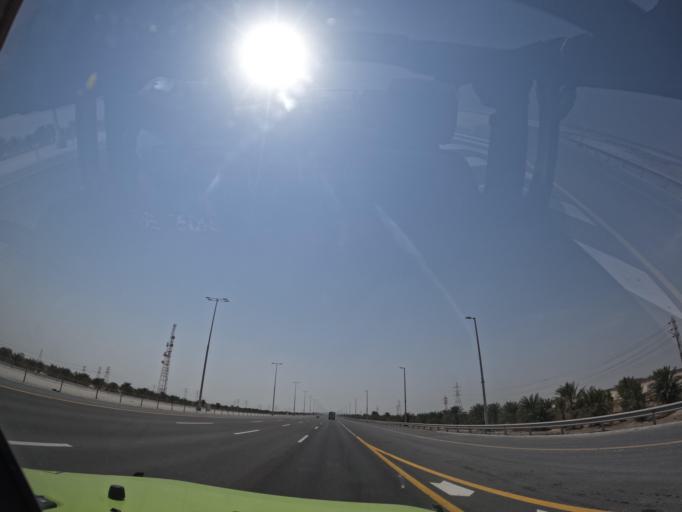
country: AE
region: Abu Dhabi
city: Abu Dhabi
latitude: 24.1768
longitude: 54.3696
